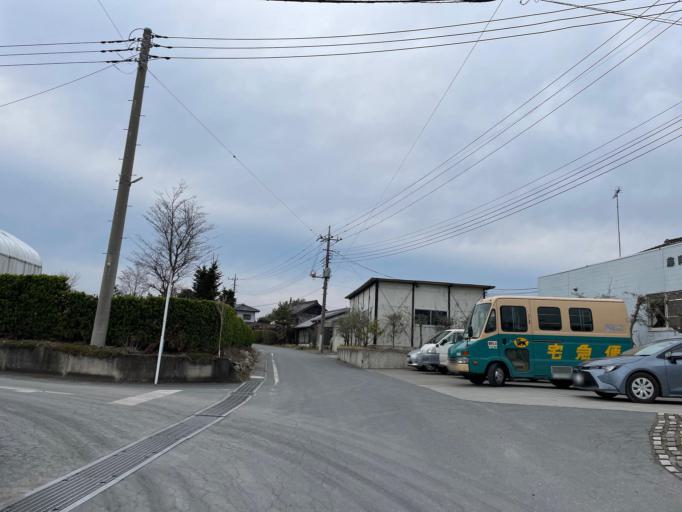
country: JP
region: Gunma
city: Fujioka
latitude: 36.2412
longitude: 139.0908
